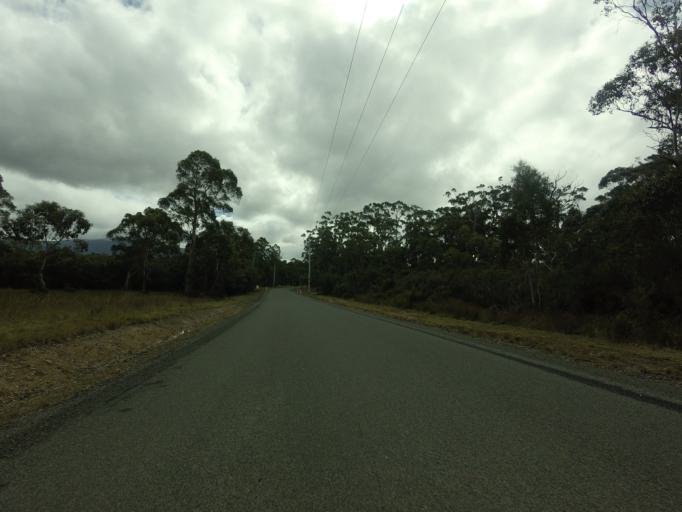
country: AU
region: Tasmania
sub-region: Huon Valley
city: Geeveston
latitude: -43.4342
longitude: 146.9037
